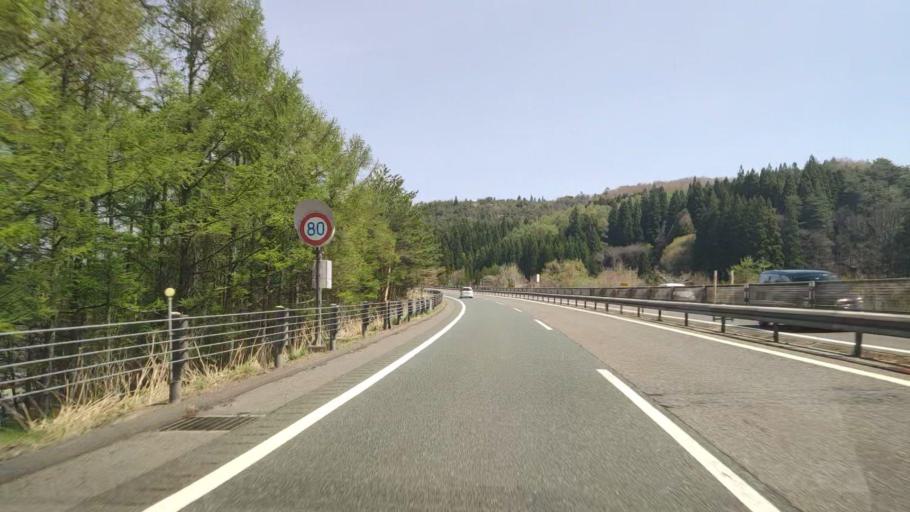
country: JP
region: Iwate
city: Ichinohe
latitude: 40.1400
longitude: 141.1144
